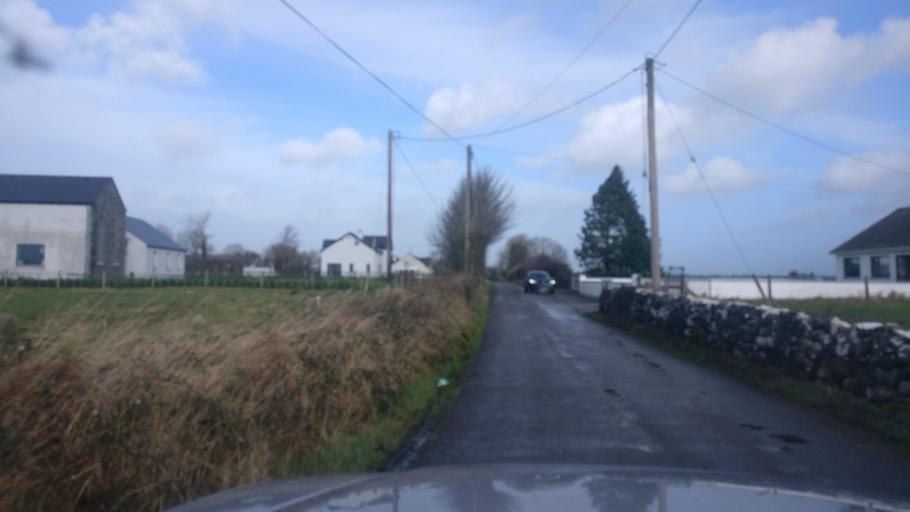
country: IE
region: Connaught
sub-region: County Galway
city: Loughrea
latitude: 53.2609
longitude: -8.5808
